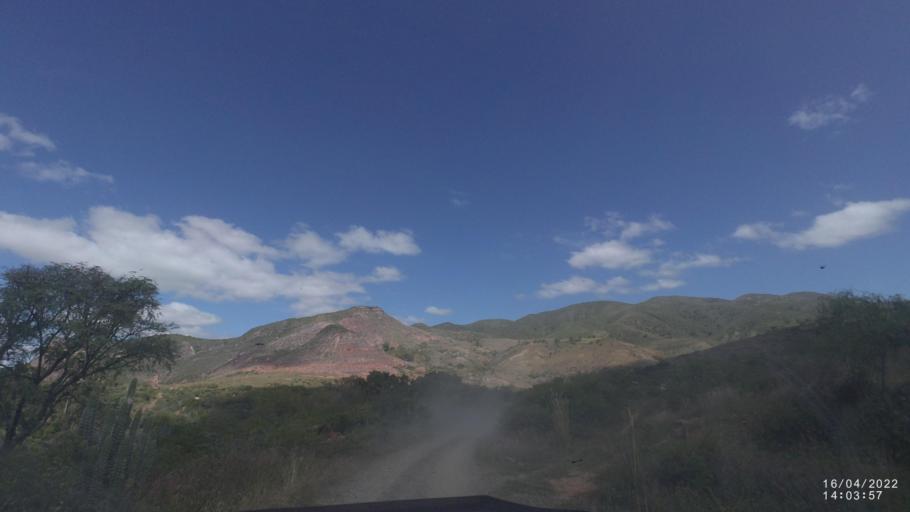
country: BO
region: Cochabamba
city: Mizque
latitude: -18.0528
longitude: -65.5407
